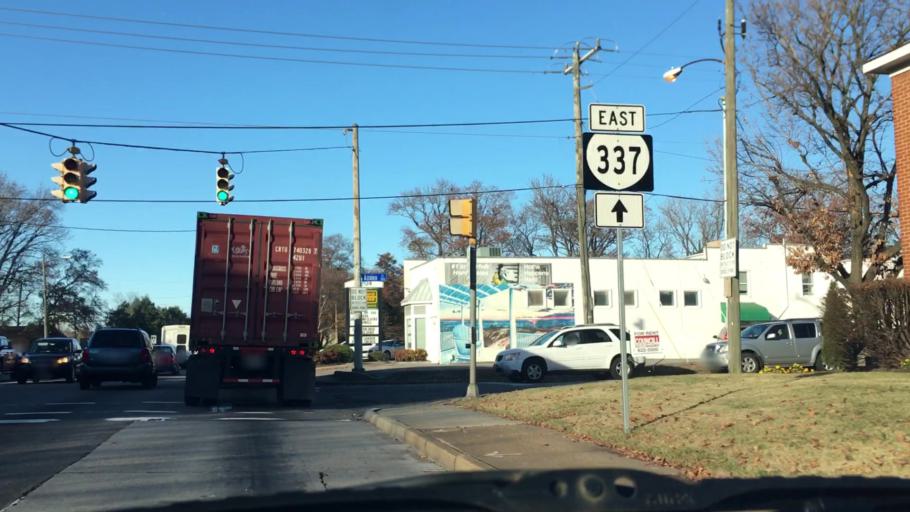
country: US
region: Virginia
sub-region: City of Norfolk
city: Norfolk
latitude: 36.8723
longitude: -76.3014
